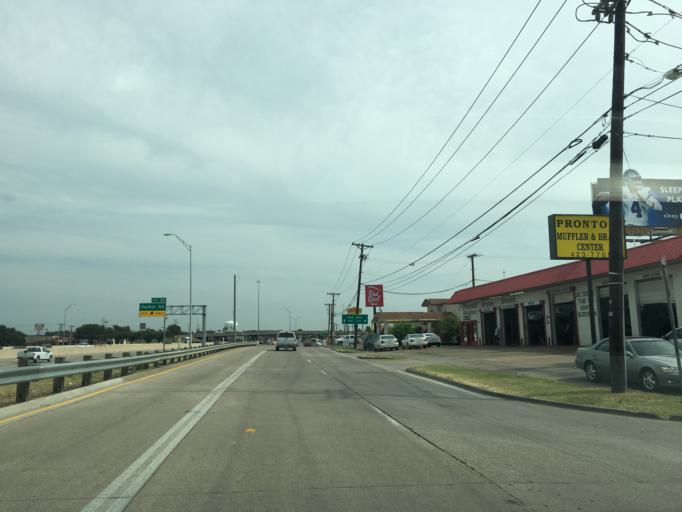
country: US
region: Texas
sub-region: Collin County
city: Plano
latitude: 33.0247
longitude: -96.7095
